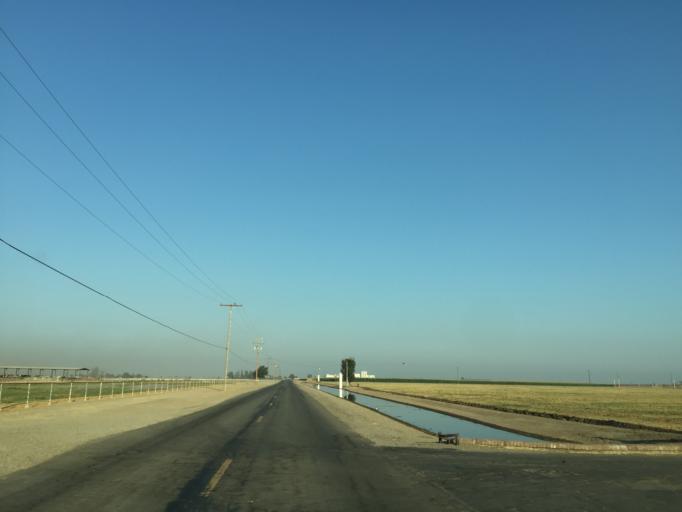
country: US
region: California
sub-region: Tulare County
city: Cutler
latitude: 36.4576
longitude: -119.2819
